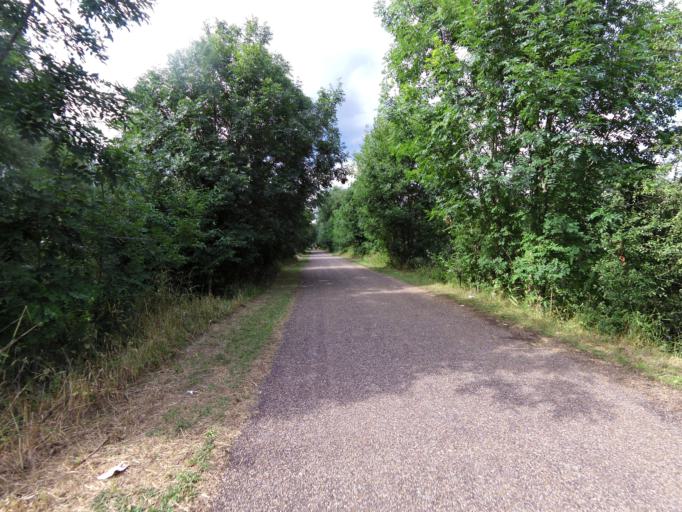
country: GB
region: England
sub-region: Essex
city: Waltham Abbey
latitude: 51.6909
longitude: -0.0119
